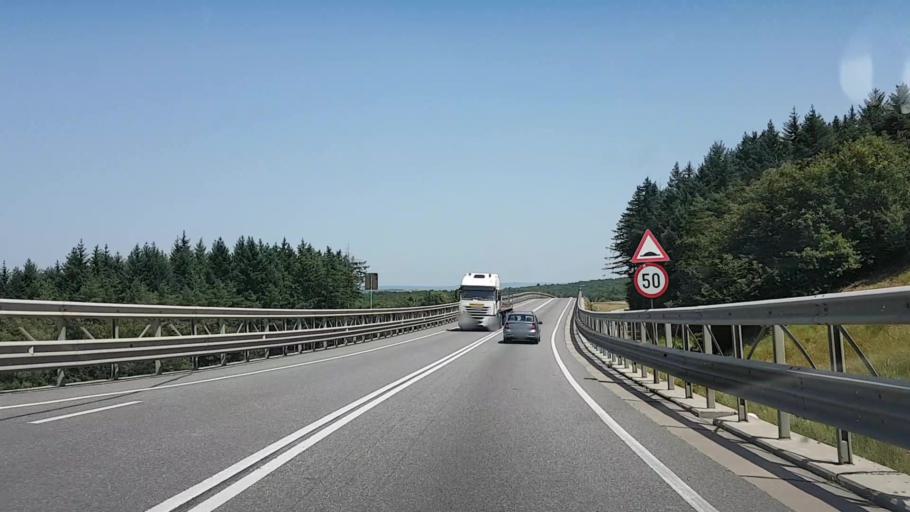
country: RO
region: Cluj
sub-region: Comuna Feleacu
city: Feleacu
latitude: 46.7283
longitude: 23.6505
